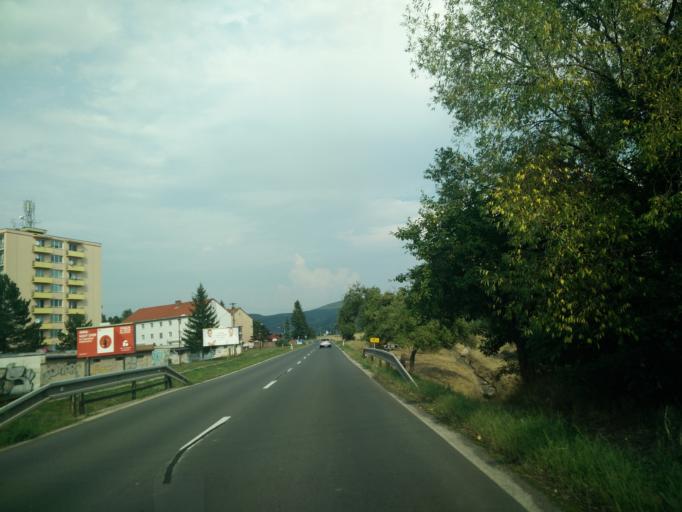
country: SK
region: Banskobystricky
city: Ziar nad Hronom
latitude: 48.5388
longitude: 18.7865
